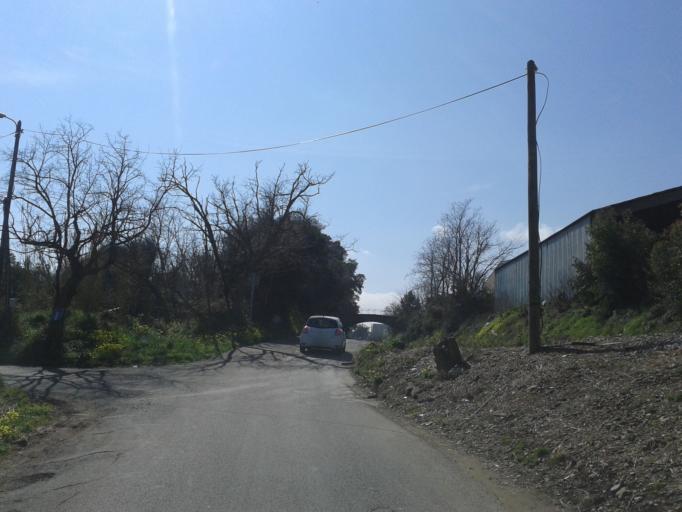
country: FR
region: Corsica
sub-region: Departement de la Haute-Corse
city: Biguglia
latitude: 42.6495
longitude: 9.4413
